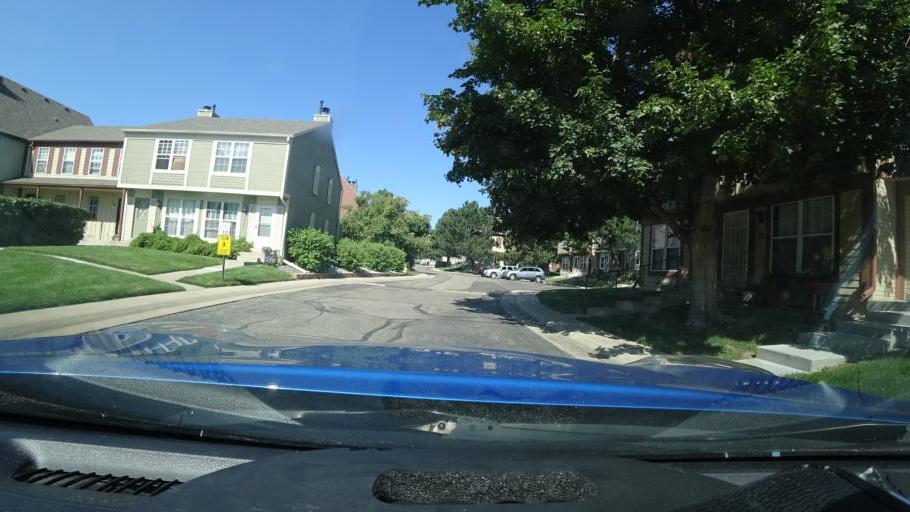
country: US
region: Colorado
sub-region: Adams County
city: Aurora
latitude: 39.6863
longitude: -104.8209
